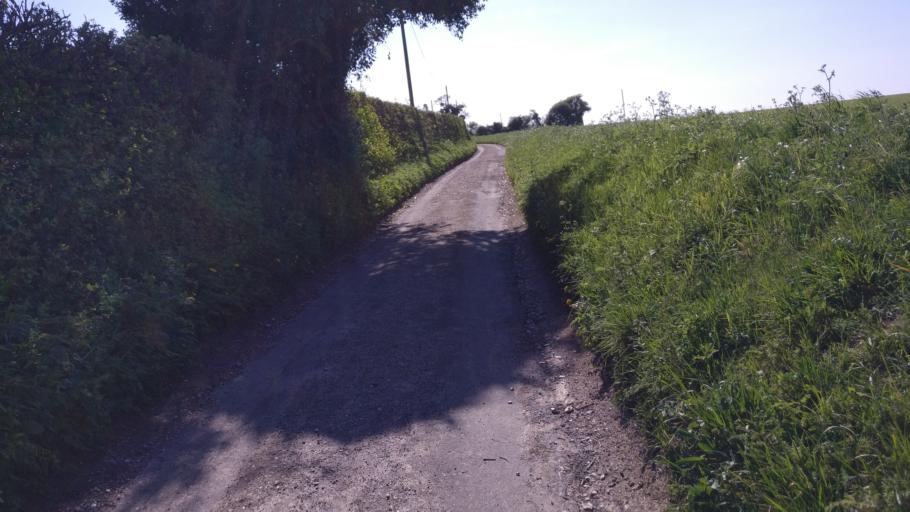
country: GB
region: England
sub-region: Hampshire
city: Basingstoke
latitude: 51.2335
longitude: -1.0875
